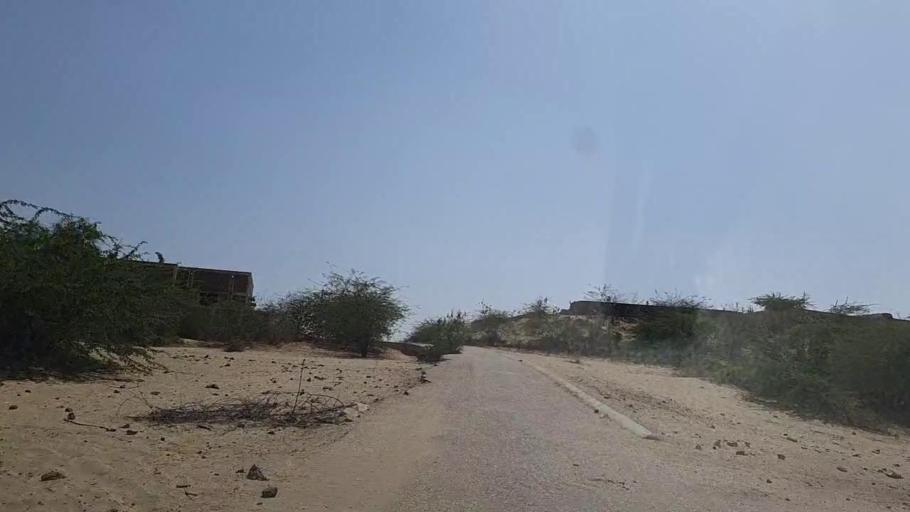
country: PK
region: Sindh
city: Diplo
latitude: 24.5103
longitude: 69.4141
